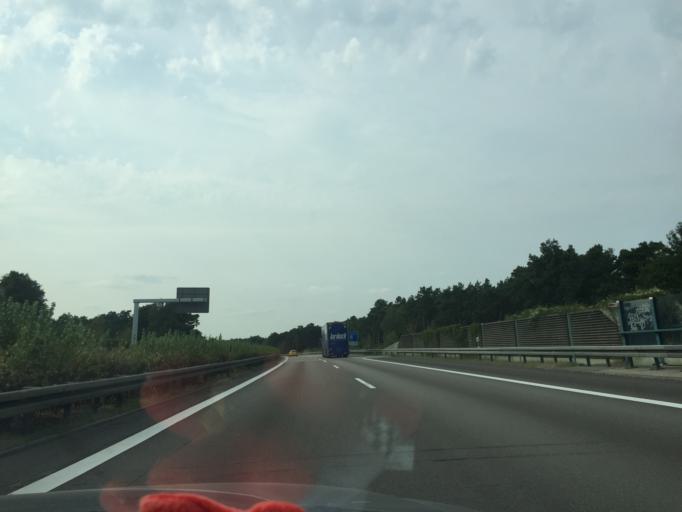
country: DE
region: Brandenburg
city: Schwerin
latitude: 52.1659
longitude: 13.6410
